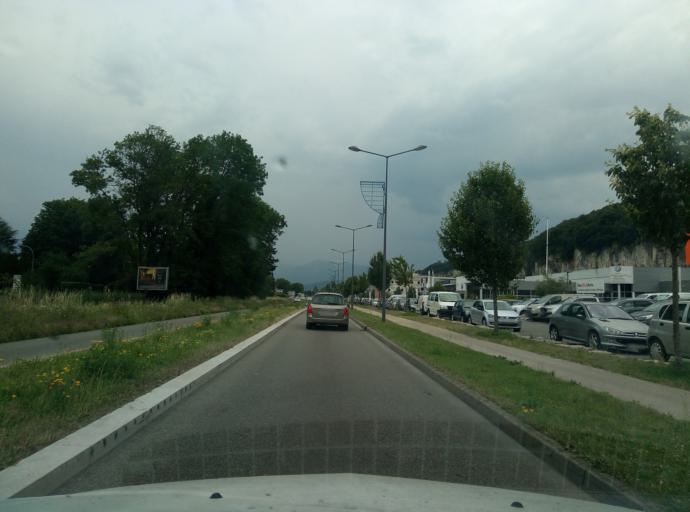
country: FR
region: Rhone-Alpes
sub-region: Departement de l'Isere
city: Fontaine
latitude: 45.1924
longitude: 5.6785
